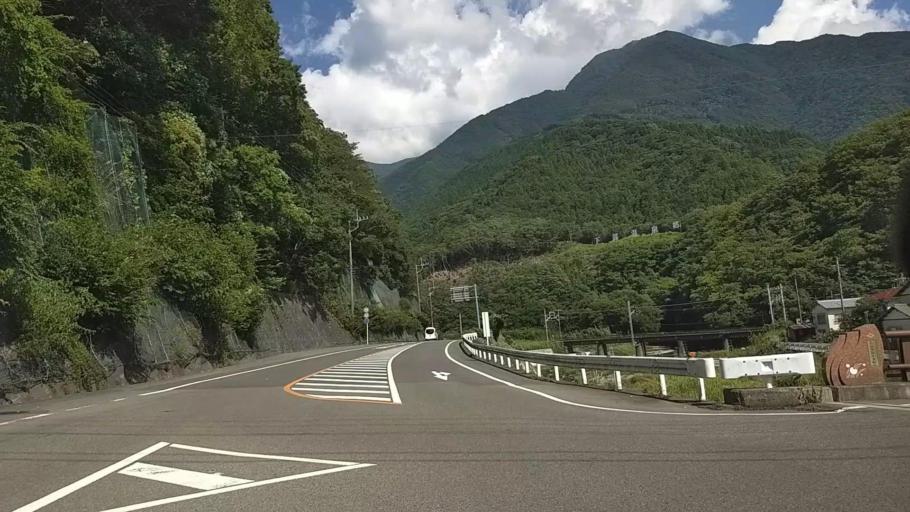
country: JP
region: Yamanashi
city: Ryuo
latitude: 35.4268
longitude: 138.4717
